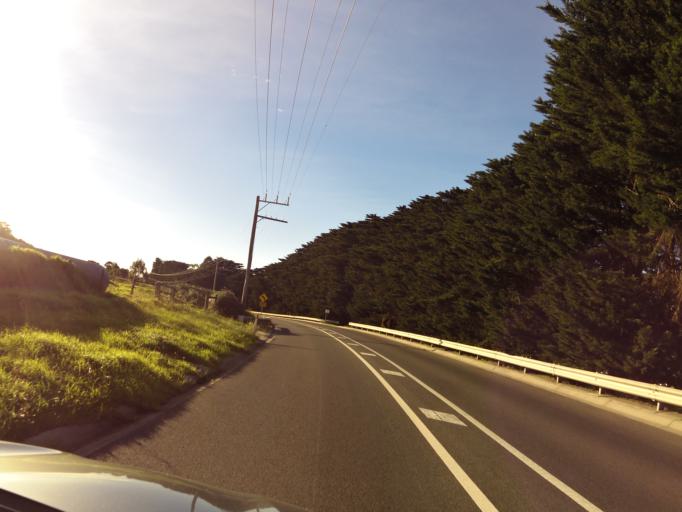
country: AU
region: Victoria
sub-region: Yarra Ranges
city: Lysterfield
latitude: -37.9184
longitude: 145.3007
